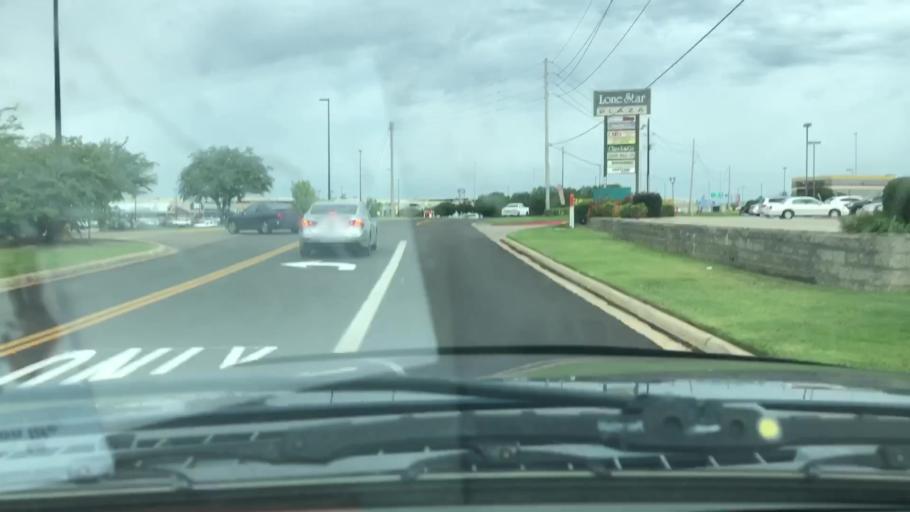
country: US
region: Texas
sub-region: Bowie County
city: Wake Village
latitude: 33.4439
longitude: -94.0993
